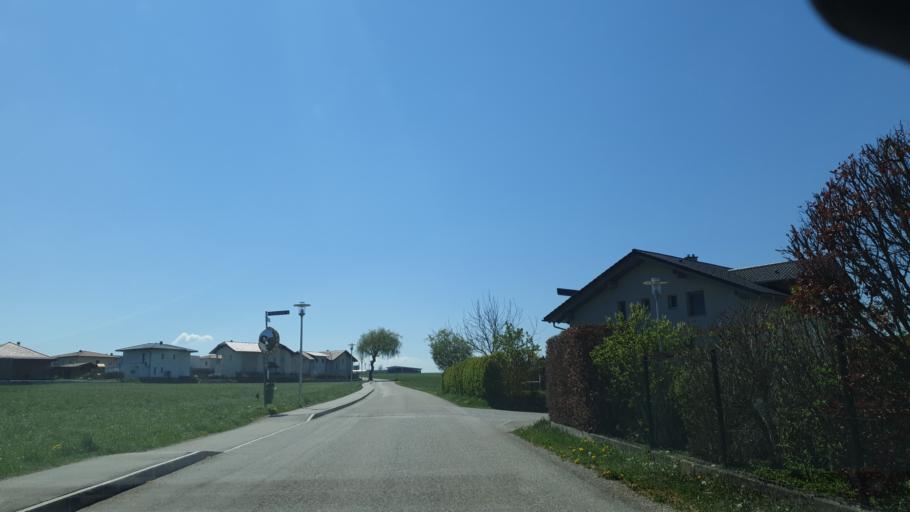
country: AT
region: Upper Austria
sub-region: Politischer Bezirk Vocklabruck
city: Gampern
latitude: 47.9859
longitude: 13.5508
